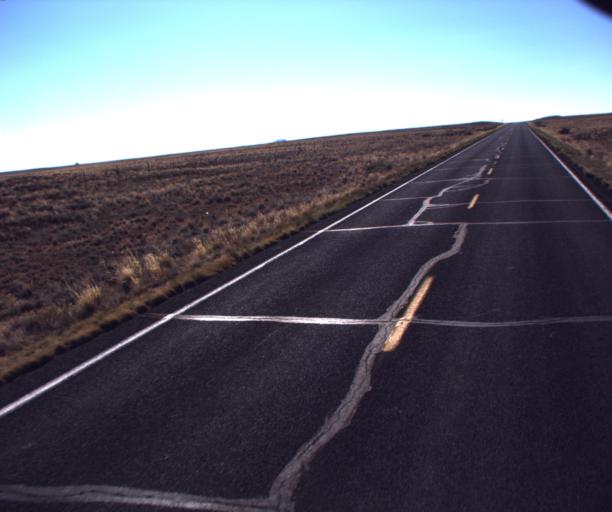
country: US
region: Arizona
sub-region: Navajo County
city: First Mesa
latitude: 35.6679
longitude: -110.4957
